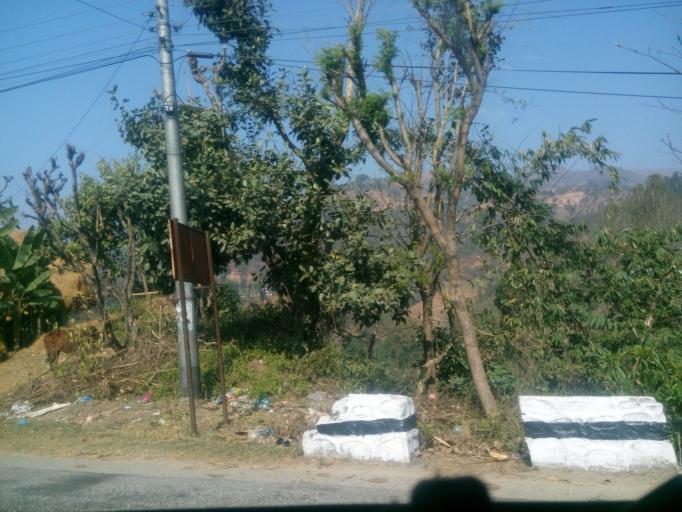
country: NP
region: Central Region
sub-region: Narayani Zone
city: Hitura
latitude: 27.8038
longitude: 84.8744
